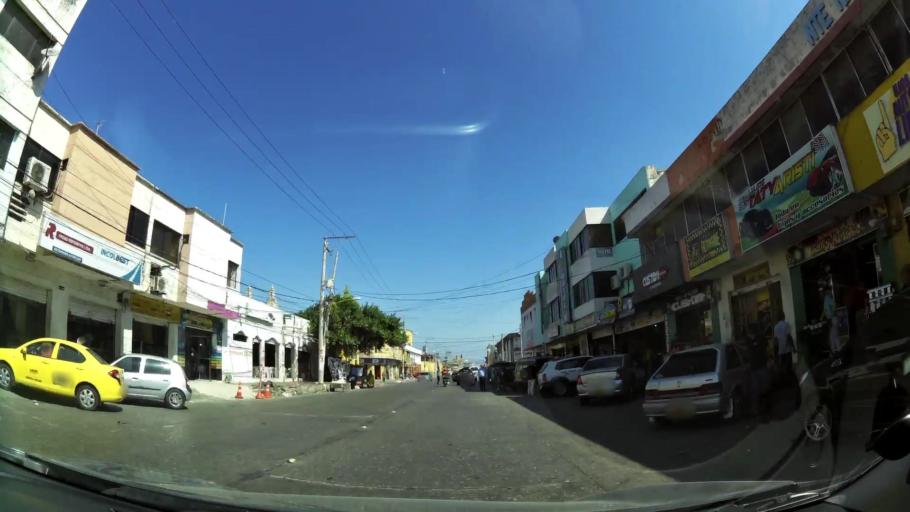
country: CO
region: Atlantico
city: Barranquilla
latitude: 10.9788
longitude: -74.7841
